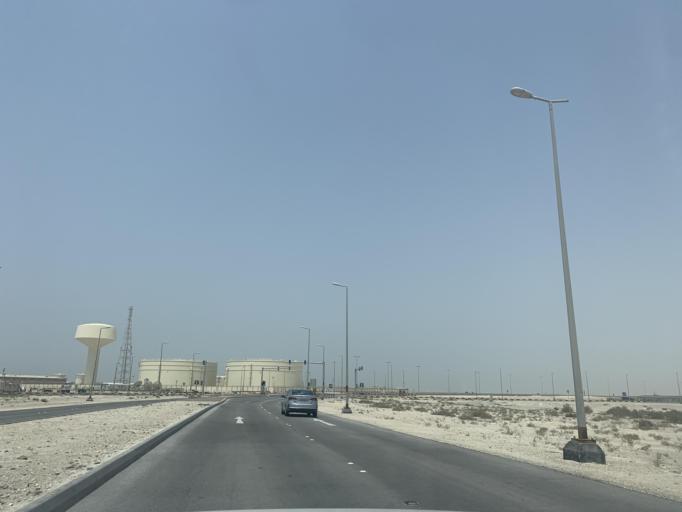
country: BH
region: Central Governorate
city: Dar Kulayb
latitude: 25.8390
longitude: 50.5890
